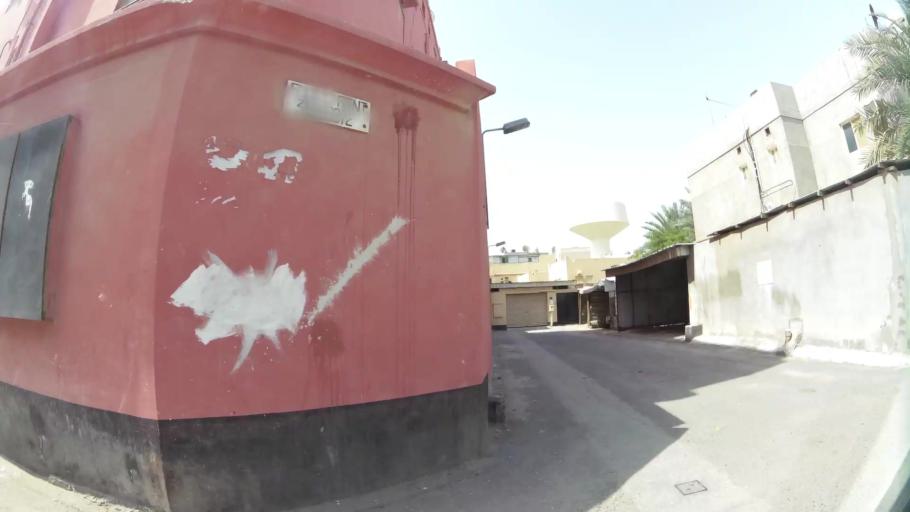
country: BH
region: Manama
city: Jidd Hafs
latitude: 26.2303
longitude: 50.4949
